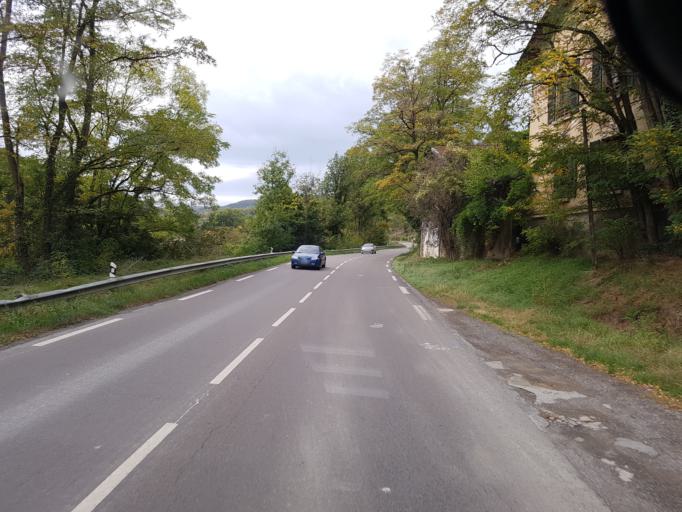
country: FR
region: Rhone-Alpes
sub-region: Departement du Rhone
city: Courzieu
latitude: 45.7450
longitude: 4.5378
